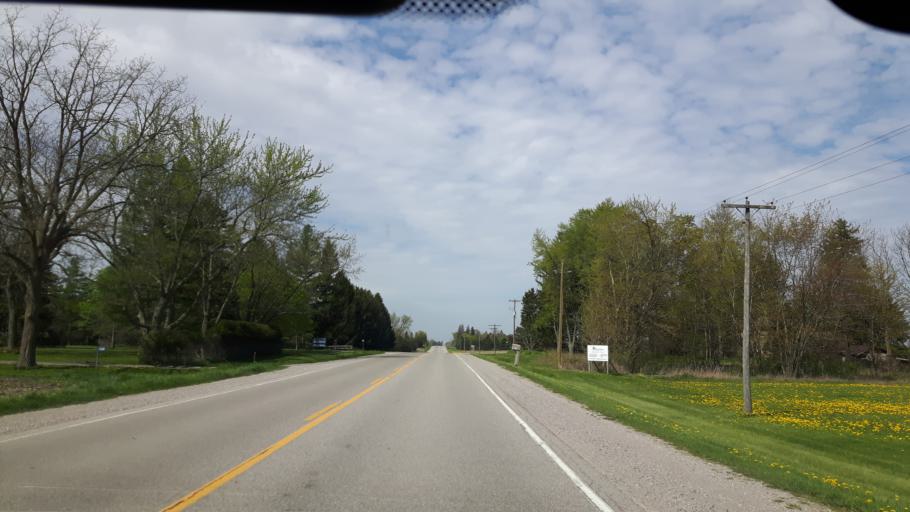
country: CA
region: Ontario
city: London
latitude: 43.0921
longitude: -81.3374
